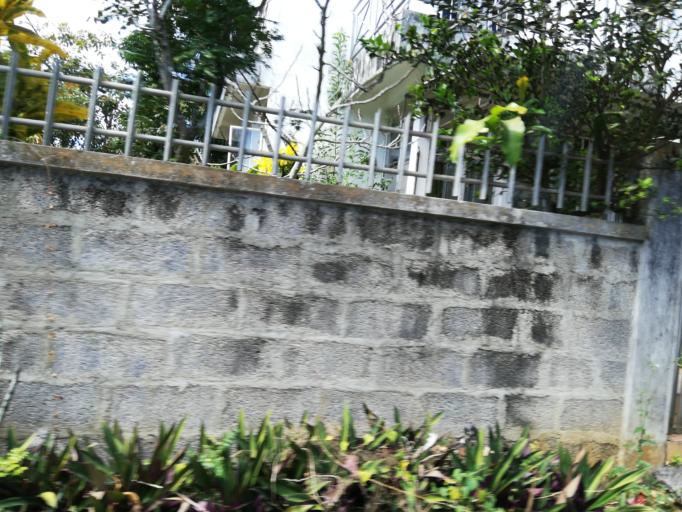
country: MU
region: Plaines Wilhems
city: Ebene
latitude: -20.2342
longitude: 57.4658
